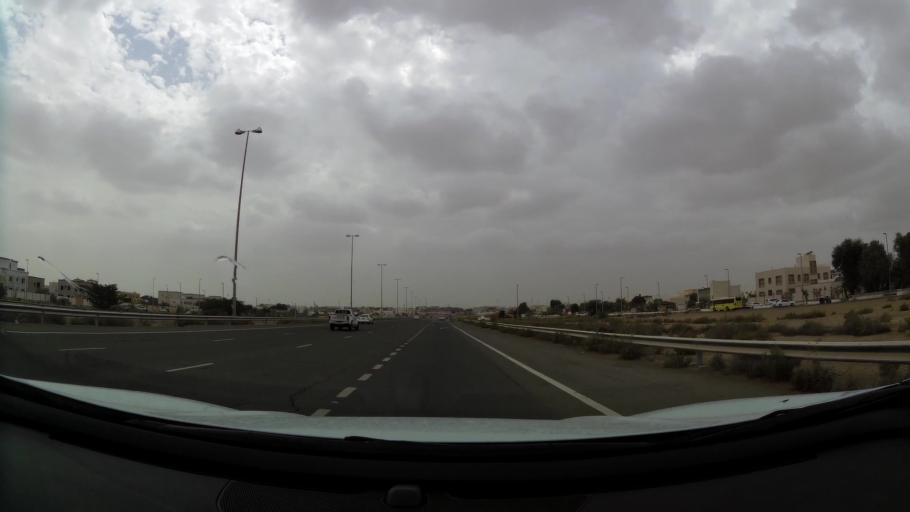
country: AE
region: Abu Dhabi
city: Abu Dhabi
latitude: 24.3307
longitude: 54.6391
